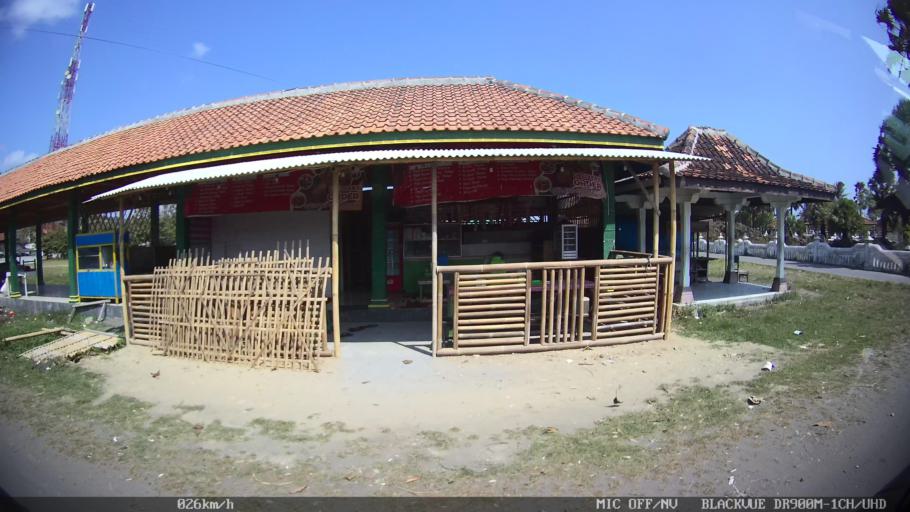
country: ID
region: Daerah Istimewa Yogyakarta
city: Pundong
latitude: -8.0198
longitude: 110.3255
